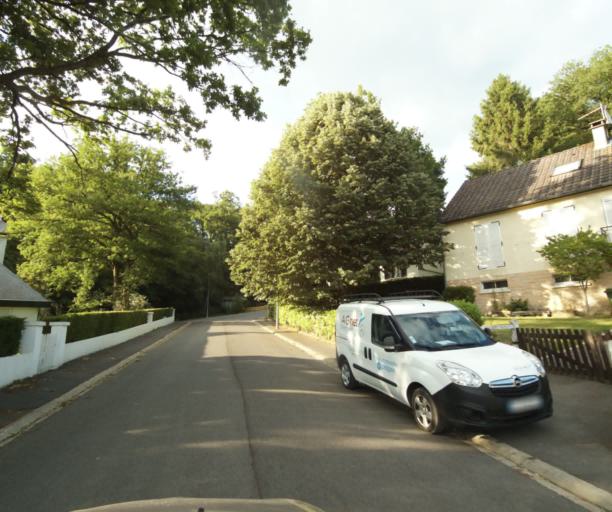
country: FR
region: Champagne-Ardenne
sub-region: Departement des Ardennes
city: Charleville-Mezieres
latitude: 49.7963
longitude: 4.7095
